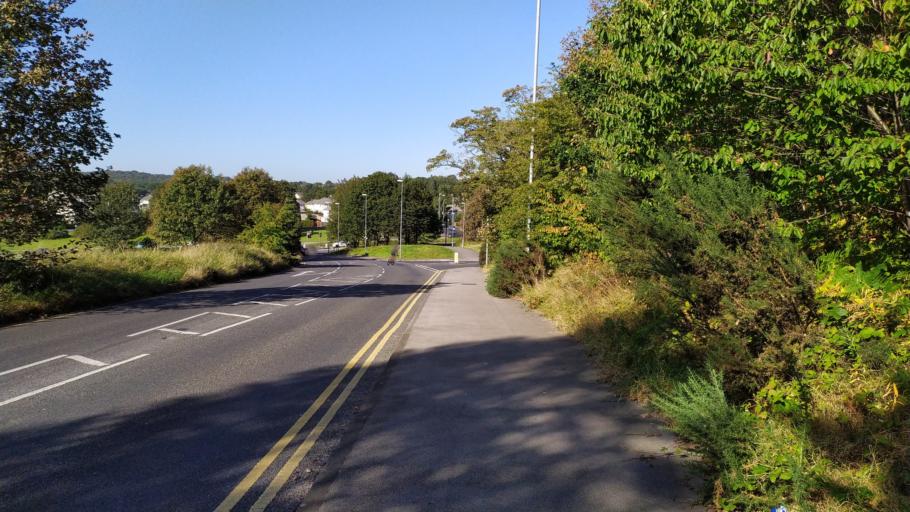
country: GB
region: England
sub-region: City and Borough of Leeds
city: Chapel Allerton
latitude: 53.8411
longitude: -1.5578
